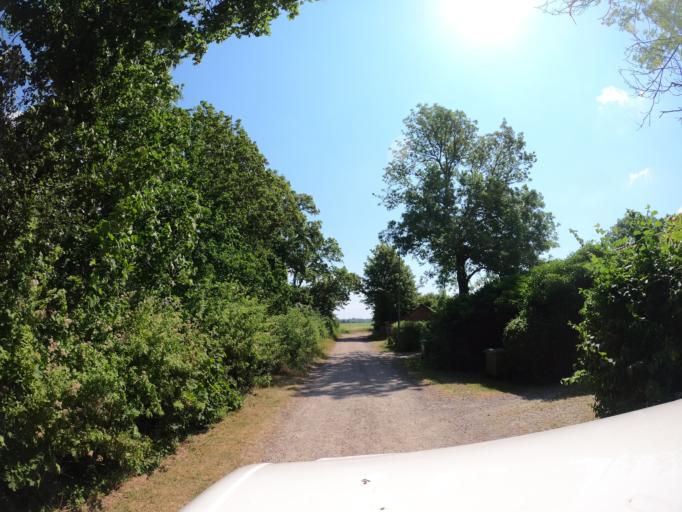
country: SE
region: Skane
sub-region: Staffanstorps Kommun
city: Hjaerup
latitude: 55.6992
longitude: 13.1430
